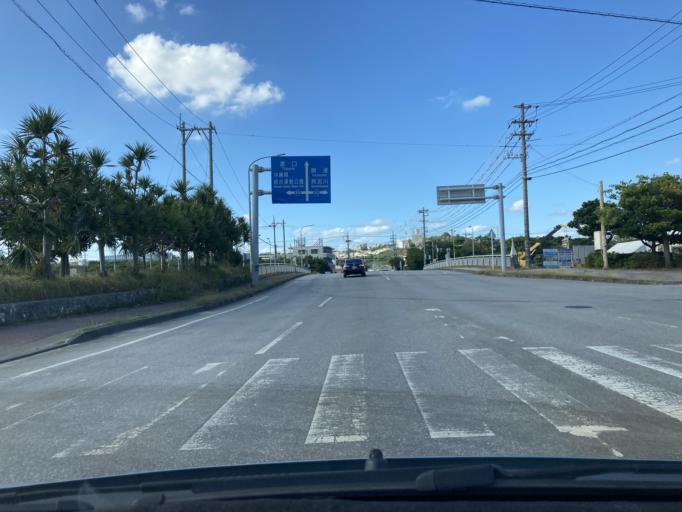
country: JP
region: Okinawa
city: Katsuren-haebaru
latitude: 26.3317
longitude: 127.8400
